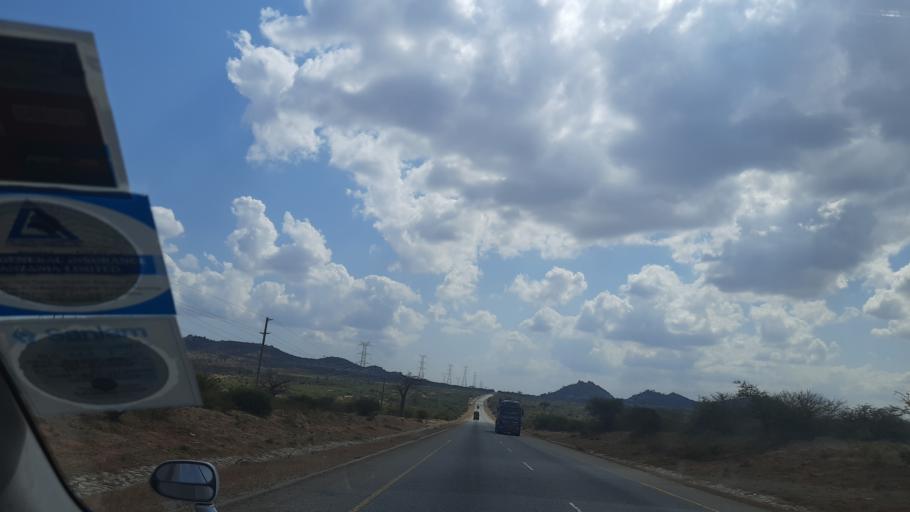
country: TZ
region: Dodoma
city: Dodoma
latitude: -6.0489
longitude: 35.5276
